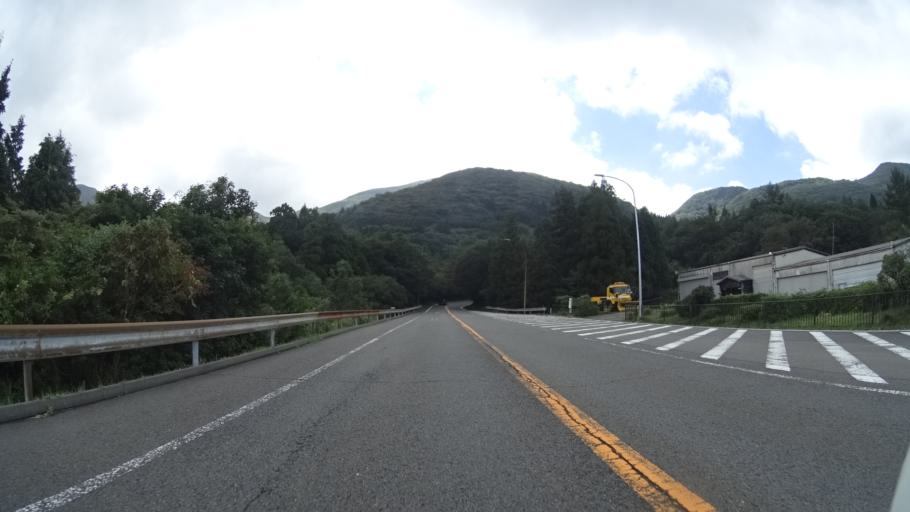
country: JP
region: Oita
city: Tsukawaki
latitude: 33.1035
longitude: 131.2218
